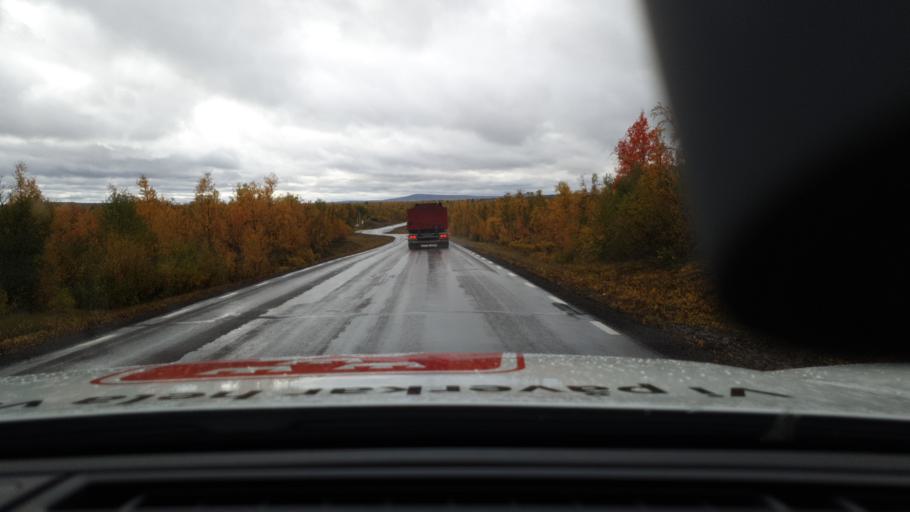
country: SE
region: Norrbotten
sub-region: Kiruna Kommun
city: Kiruna
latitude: 67.7893
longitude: 20.2298
